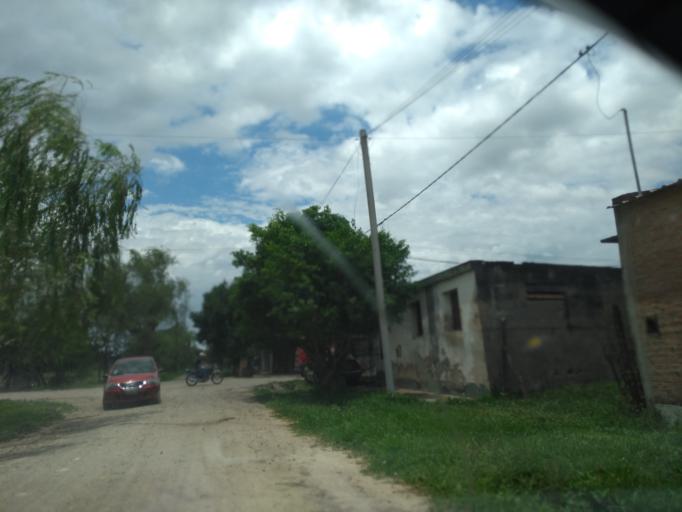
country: AR
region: Chaco
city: Resistencia
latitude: -27.4711
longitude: -58.9732
